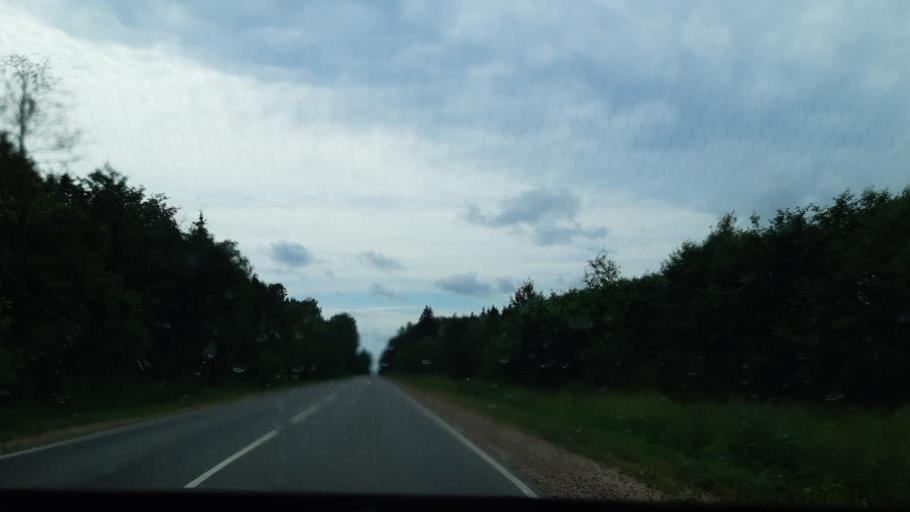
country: RU
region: Moskovskaya
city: Vereya
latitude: 55.3816
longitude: 36.2903
